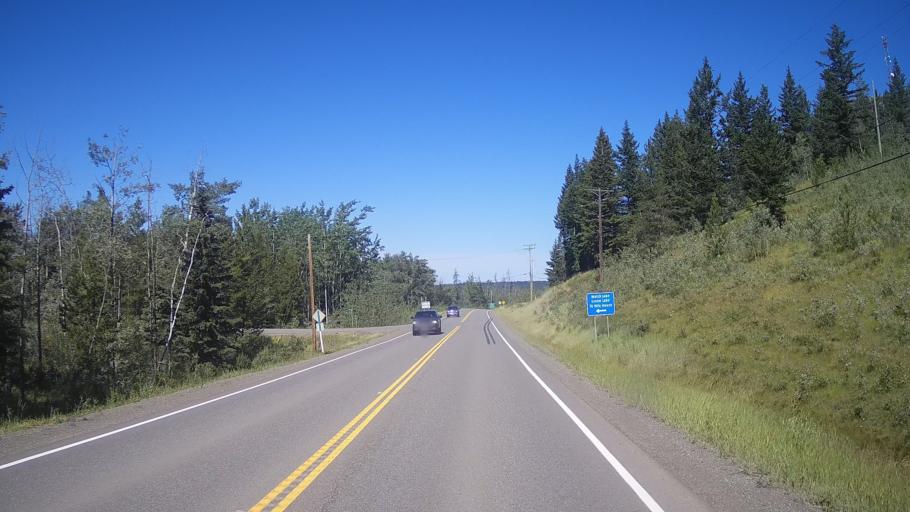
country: CA
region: British Columbia
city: Cache Creek
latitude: 51.5518
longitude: -121.1866
